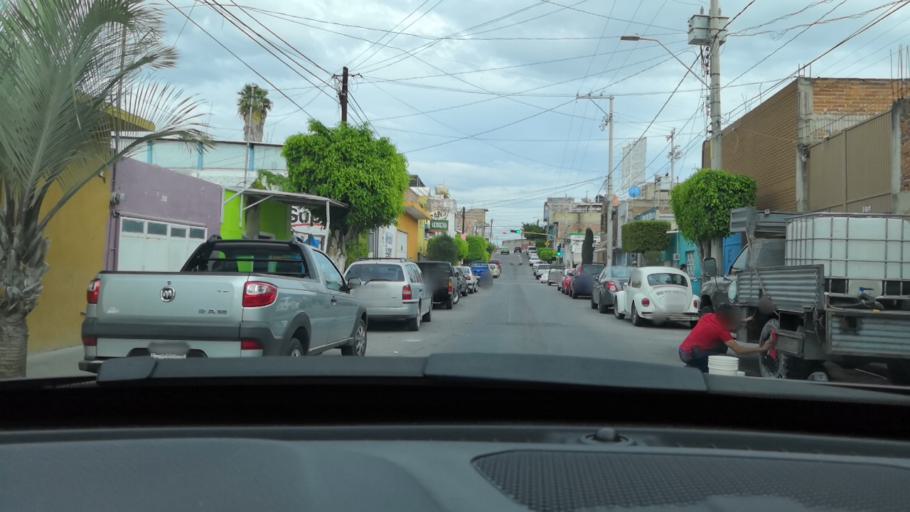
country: MX
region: Guanajuato
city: Leon
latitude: 21.1278
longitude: -101.7061
